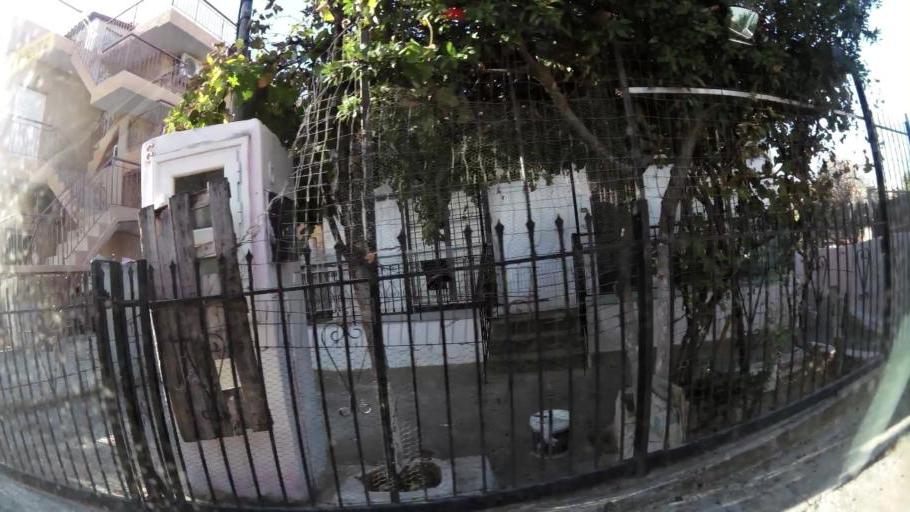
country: GR
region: Attica
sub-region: Nomarchia Anatolikis Attikis
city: Acharnes
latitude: 38.0761
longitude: 23.7476
